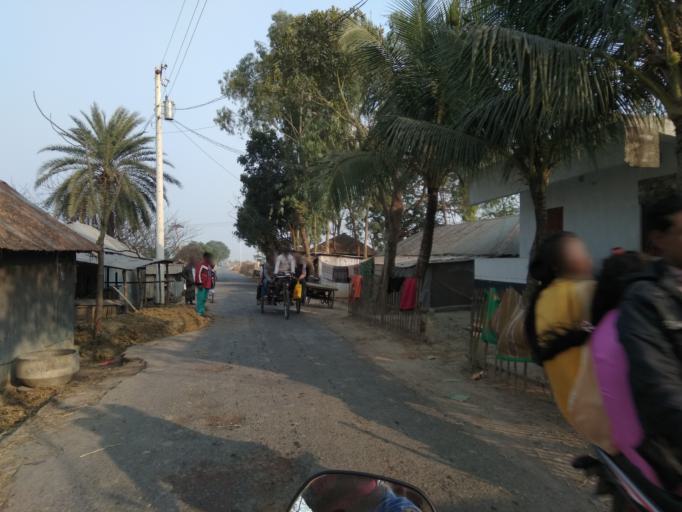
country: BD
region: Rajshahi
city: Par Naogaon
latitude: 24.4989
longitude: 89.1548
